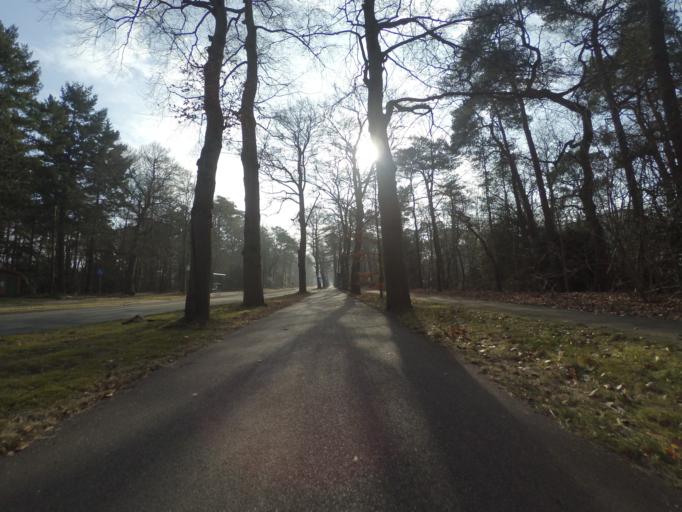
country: NL
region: Utrecht
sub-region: Gemeente Zeist
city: Zeist
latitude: 52.0790
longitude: 5.2498
